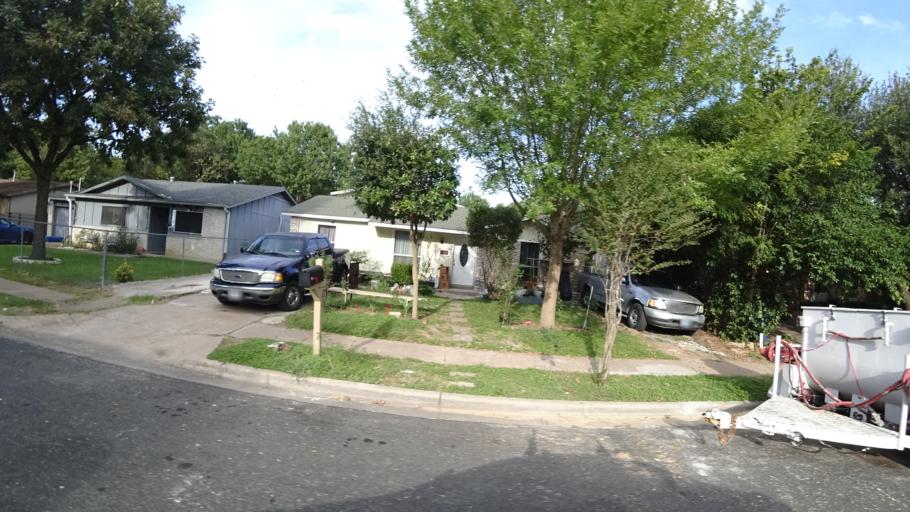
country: US
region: Texas
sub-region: Travis County
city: Onion Creek
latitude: 30.1878
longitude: -97.7521
